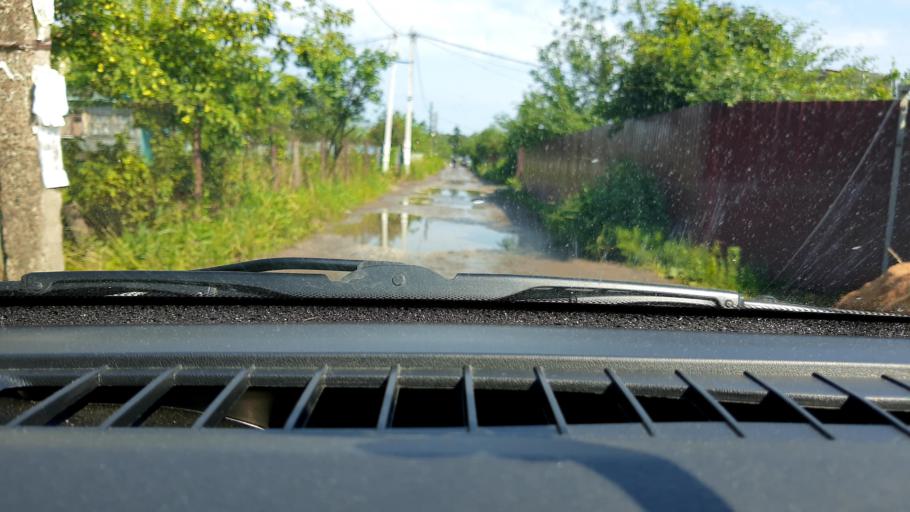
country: RU
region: Nizjnij Novgorod
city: Gorbatovka
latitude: 56.3171
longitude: 43.8294
